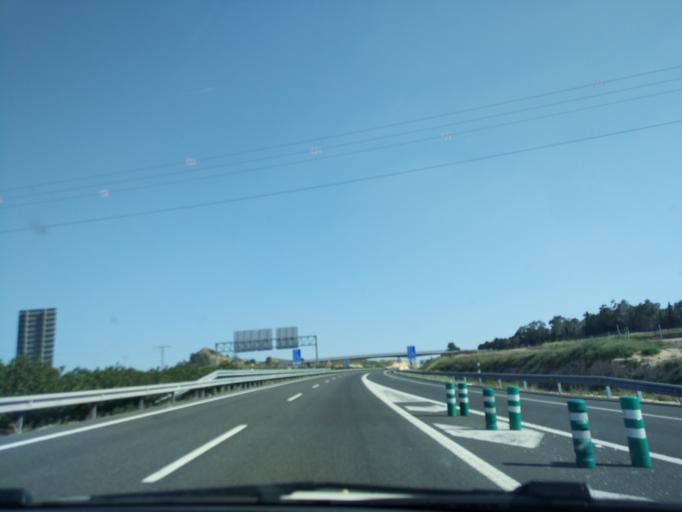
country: ES
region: Murcia
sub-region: Murcia
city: Ojos
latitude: 38.1827
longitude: -1.3191
